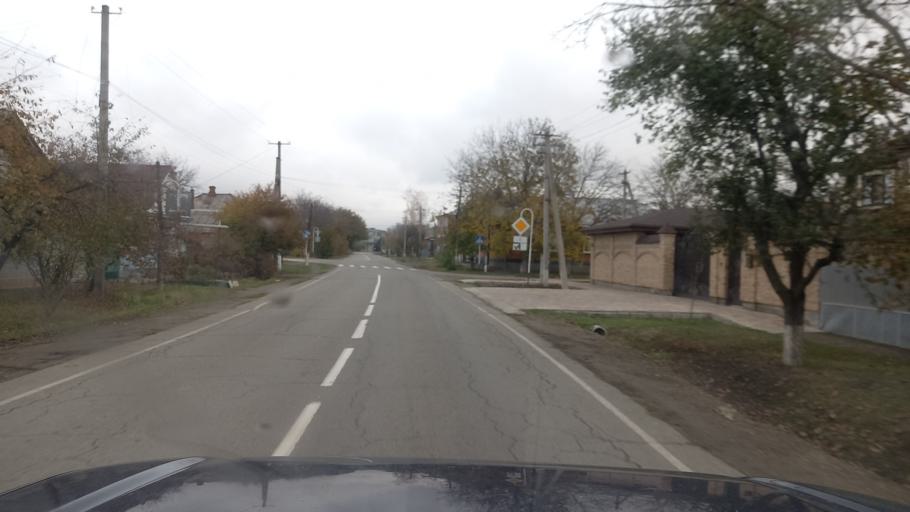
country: RU
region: Adygeya
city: Maykop
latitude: 44.6071
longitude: 40.0801
